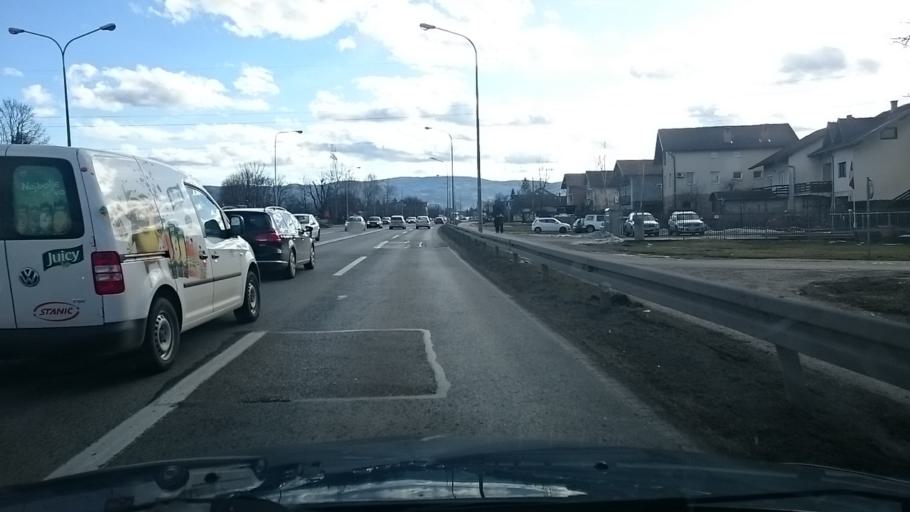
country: BA
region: Republika Srpska
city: Banja Luka
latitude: 44.8024
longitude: 17.1985
